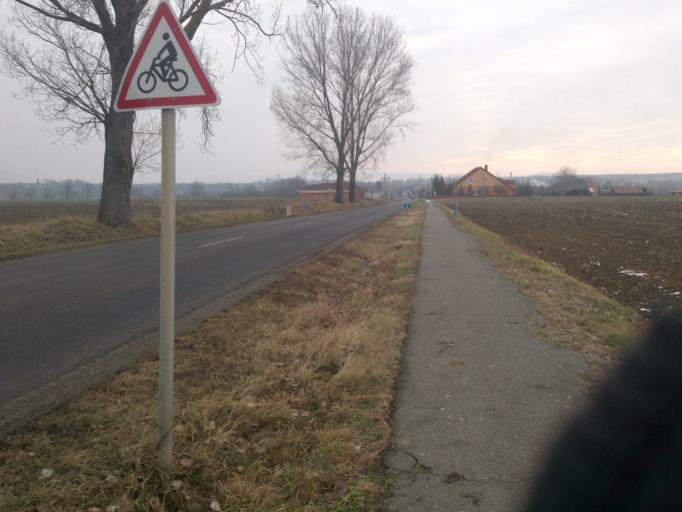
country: HU
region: Borsod-Abauj-Zemplen
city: Encs
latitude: 48.3210
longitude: 21.1517
